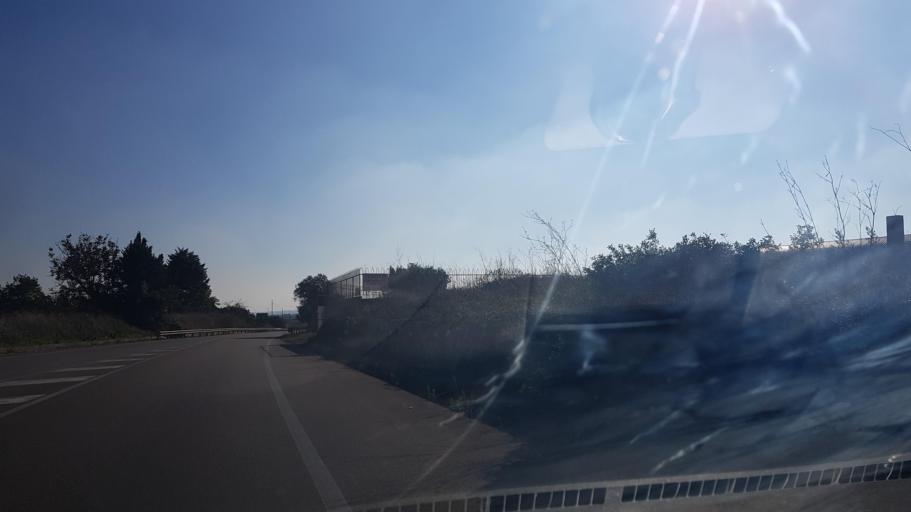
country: IT
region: Apulia
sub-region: Provincia di Lecce
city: Nociglia
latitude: 40.0443
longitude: 18.3224
